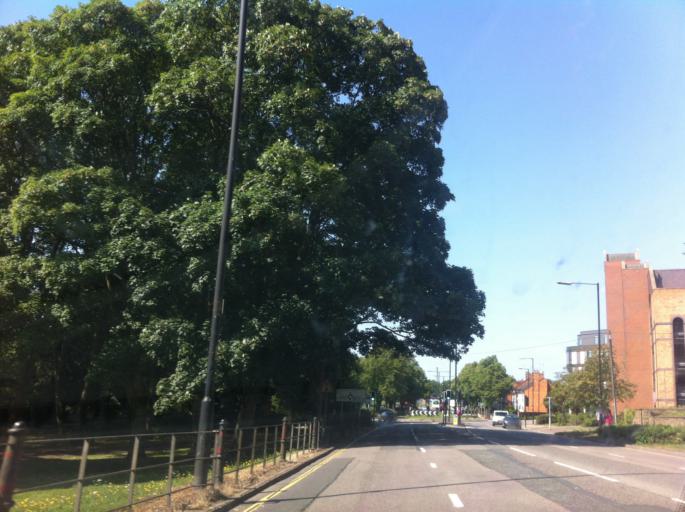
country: GB
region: England
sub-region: Northamptonshire
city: Northampton
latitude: 52.2353
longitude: -0.8891
